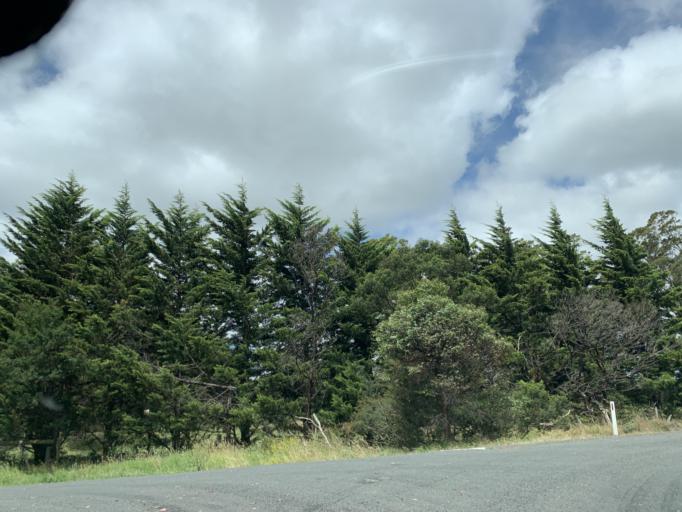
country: AU
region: Victoria
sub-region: Latrobe
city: Traralgon
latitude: -38.1139
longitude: 146.5559
